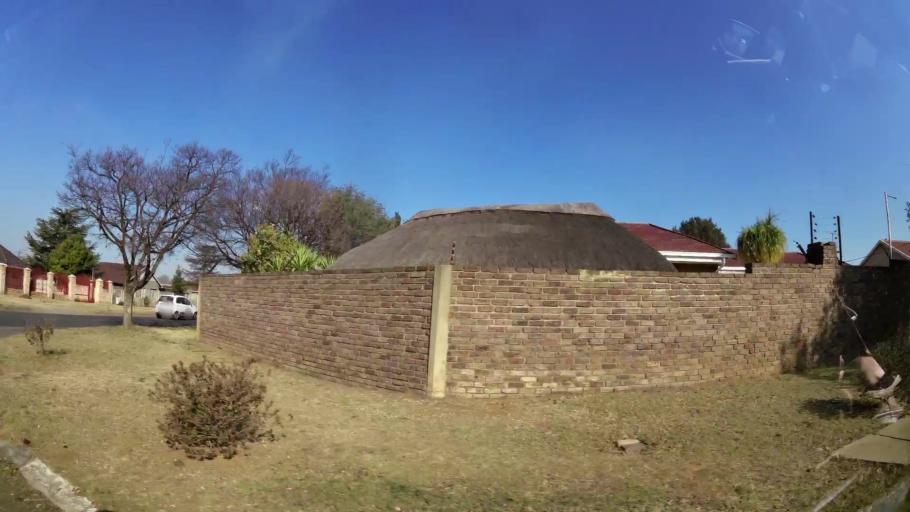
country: ZA
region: Gauteng
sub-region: West Rand District Municipality
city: Randfontein
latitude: -26.1846
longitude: 27.6808
